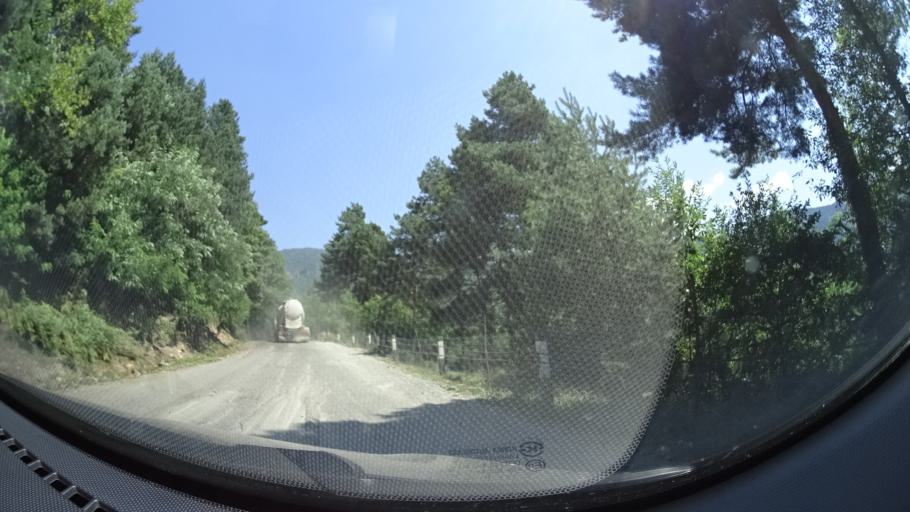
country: GE
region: Ajaria
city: Khulo
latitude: 41.6334
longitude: 42.2985
